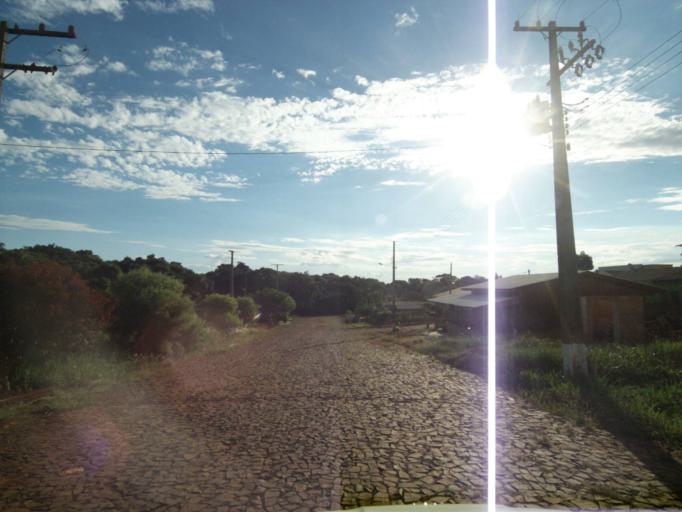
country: BR
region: Parana
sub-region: Laranjeiras Do Sul
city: Laranjeiras do Sul
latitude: -25.4957
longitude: -52.5330
